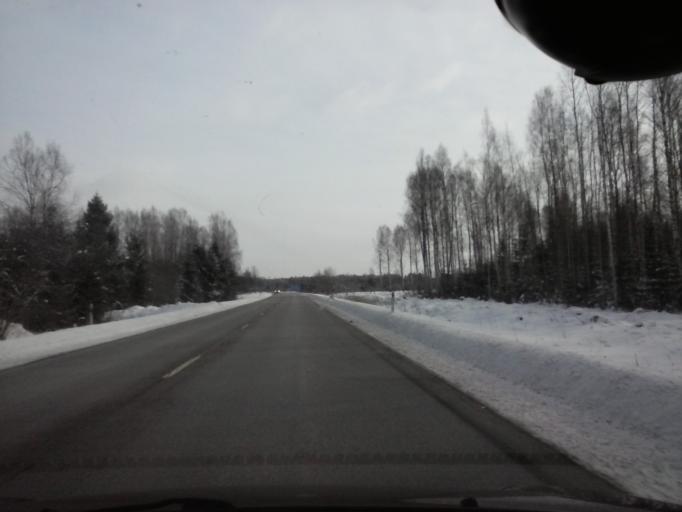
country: EE
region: Paernumaa
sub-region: Saarde vald
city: Kilingi-Nomme
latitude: 58.1734
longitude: 24.8090
